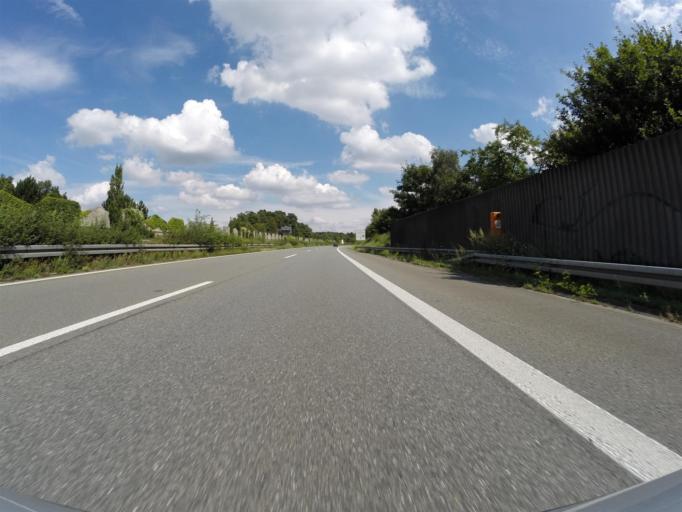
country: DE
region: North Rhine-Westphalia
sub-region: Regierungsbezirk Detmold
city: Oerlinghausen
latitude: 51.9143
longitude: 8.6188
